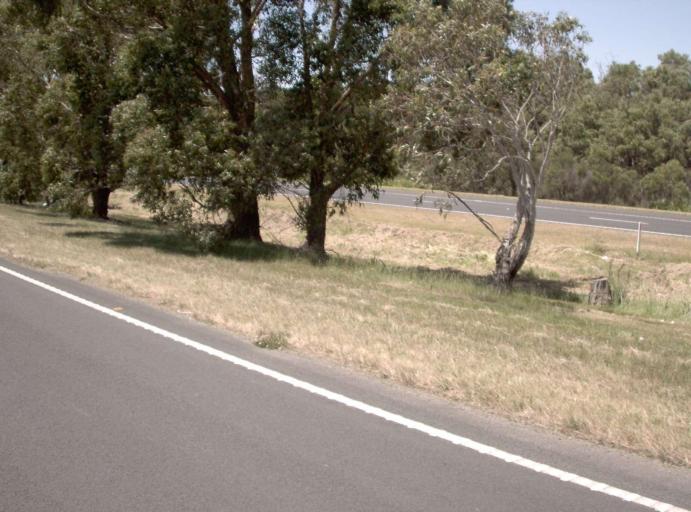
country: AU
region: Victoria
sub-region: Cardinia
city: Bunyip
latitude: -38.0750
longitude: 145.7199
